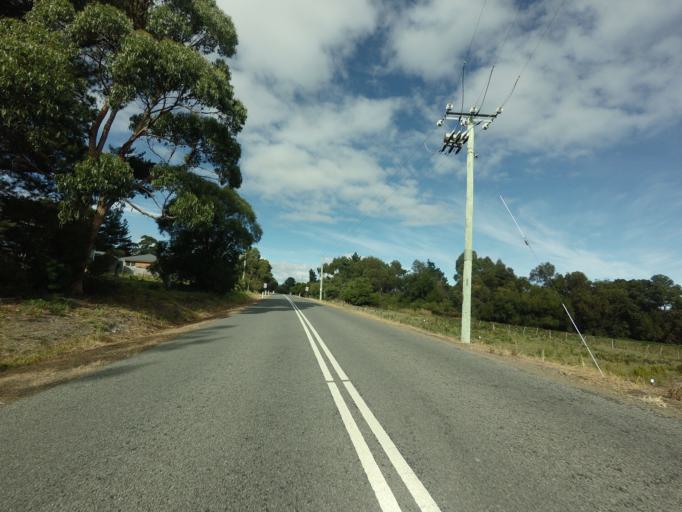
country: AU
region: Tasmania
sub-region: Clarence
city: Sandford
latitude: -43.0873
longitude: 147.7376
